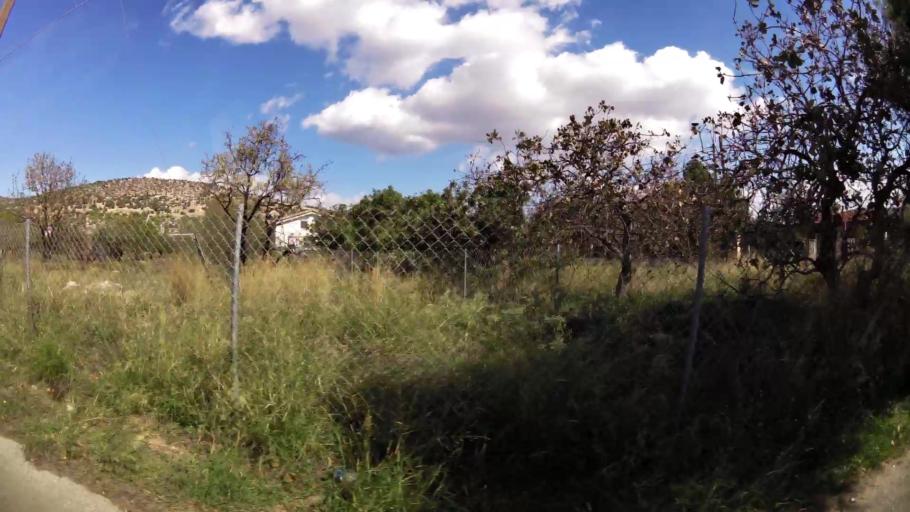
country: GR
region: Attica
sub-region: Nomarchia Anatolikis Attikis
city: Vari
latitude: 37.8396
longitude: 23.8016
